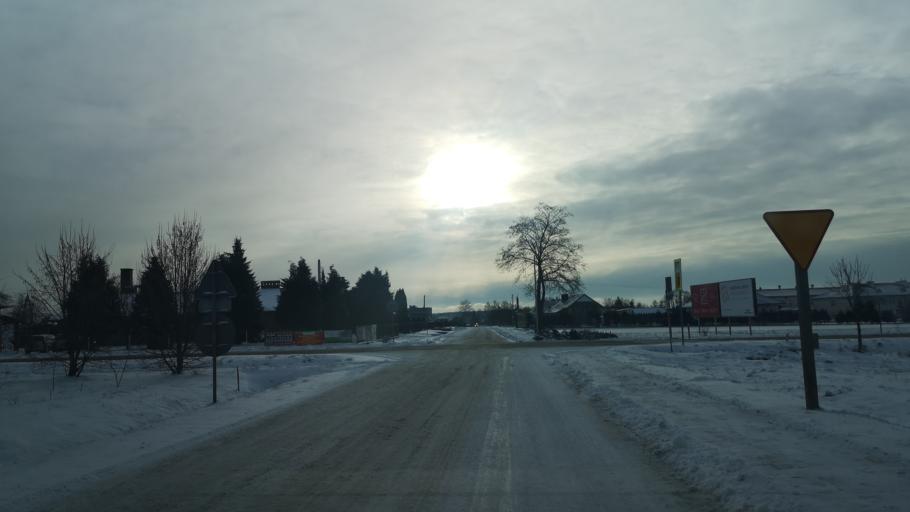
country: PL
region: Subcarpathian Voivodeship
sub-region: Powiat przeworski
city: Adamowka
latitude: 50.2577
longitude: 22.6963
